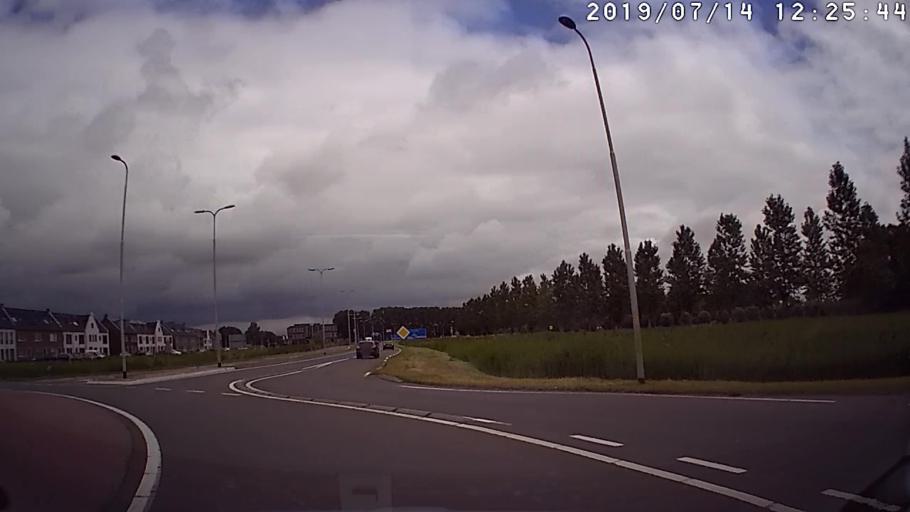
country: NL
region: Overijssel
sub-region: Gemeente Kampen
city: Kampen
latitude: 52.5332
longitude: 5.9198
